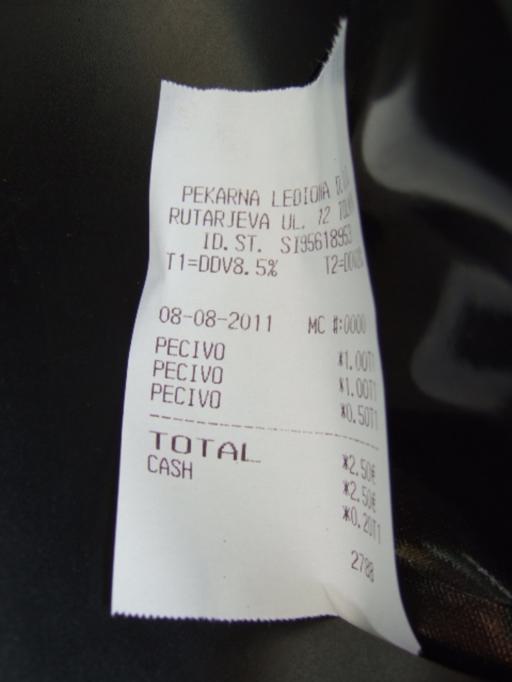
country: SI
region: Tolmin
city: Tolmin
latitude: 46.1837
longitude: 13.7367
